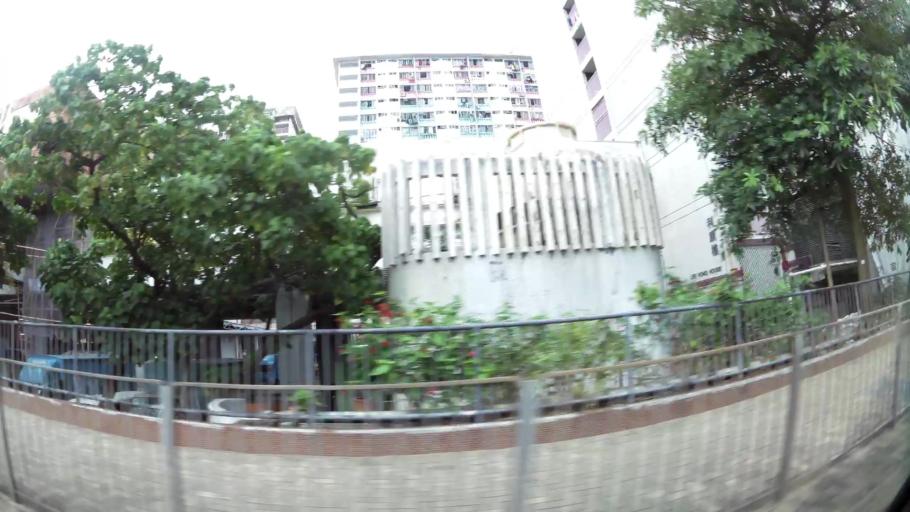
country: HK
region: Kowloon City
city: Kowloon
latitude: 22.3308
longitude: 114.2256
